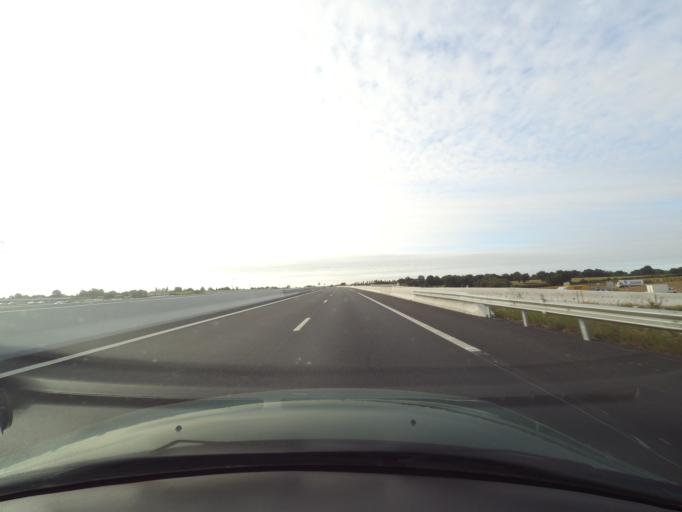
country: FR
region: Pays de la Loire
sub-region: Departement de Maine-et-Loire
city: Cholet
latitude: 47.0378
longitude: -0.9057
